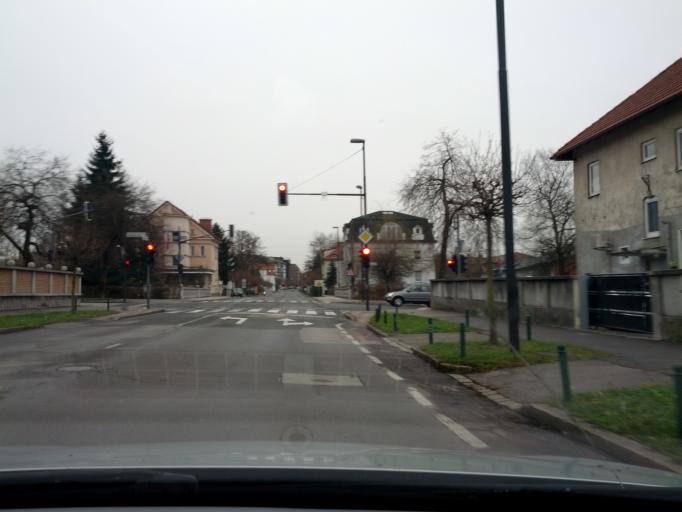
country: SI
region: Ljubljana
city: Ljubljana
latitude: 46.0442
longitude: 14.4973
